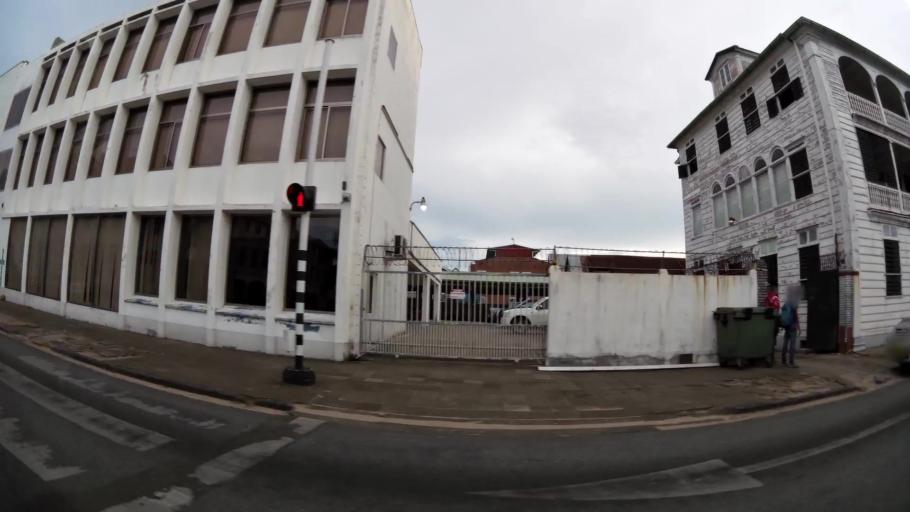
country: SR
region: Paramaribo
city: Paramaribo
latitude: 5.8282
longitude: -55.1539
